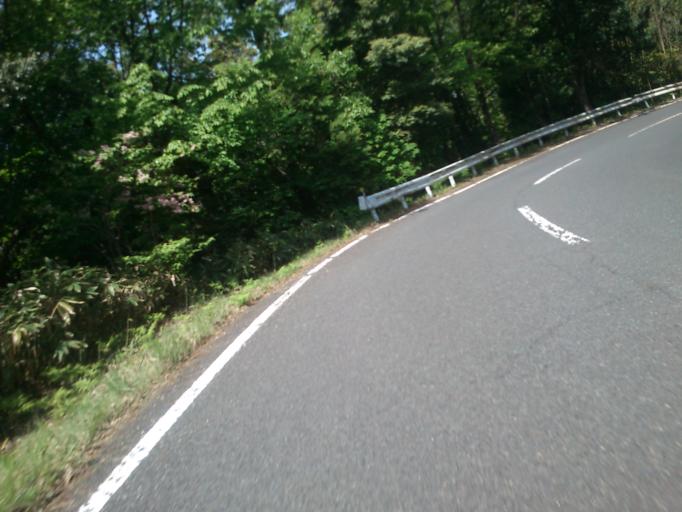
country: JP
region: Kyoto
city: Miyazu
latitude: 35.6303
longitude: 135.2163
